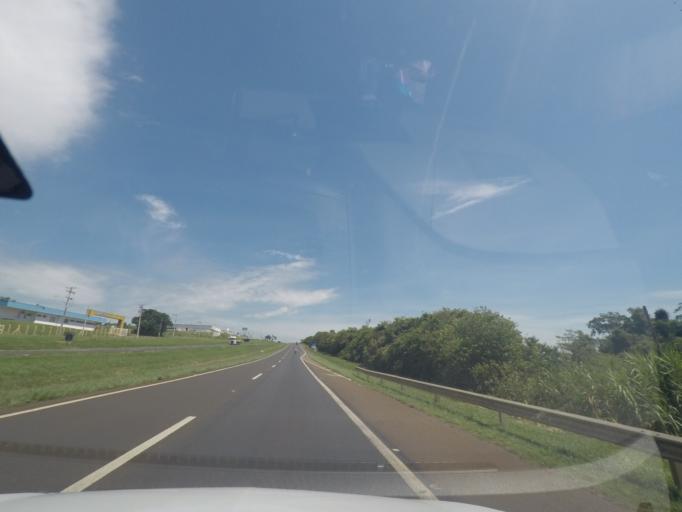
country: BR
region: Sao Paulo
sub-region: Araraquara
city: Araraquara
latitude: -21.7730
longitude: -48.2374
